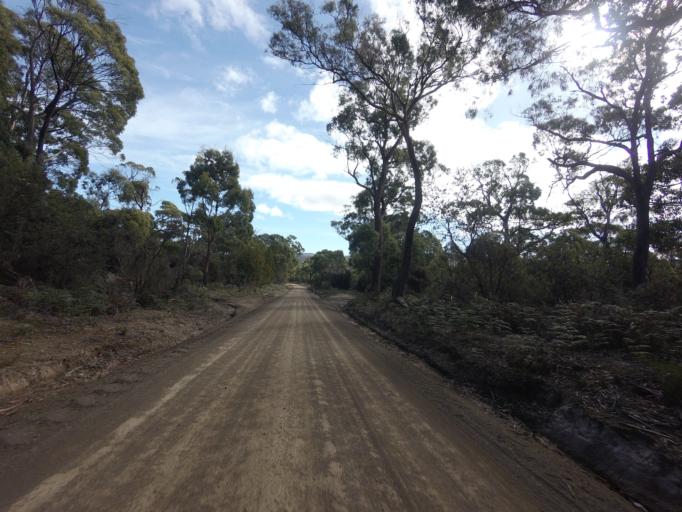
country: AU
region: Tasmania
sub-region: Clarence
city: Sandford
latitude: -43.0883
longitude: 147.6988
